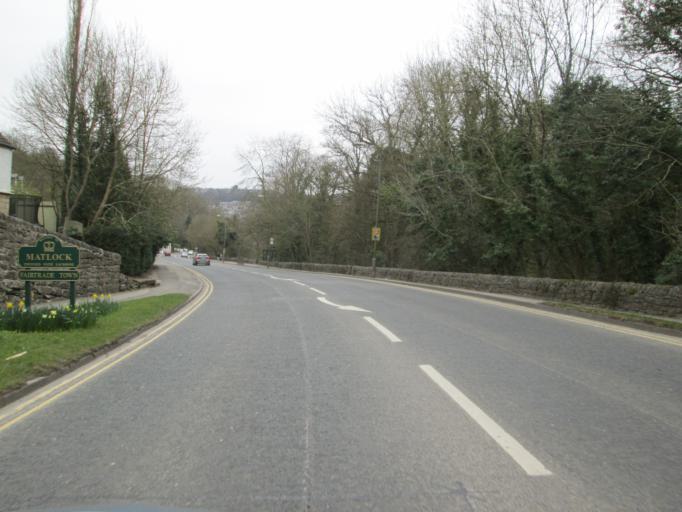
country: GB
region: England
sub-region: Derbyshire
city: Matlock
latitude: 53.1327
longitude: -1.5573
